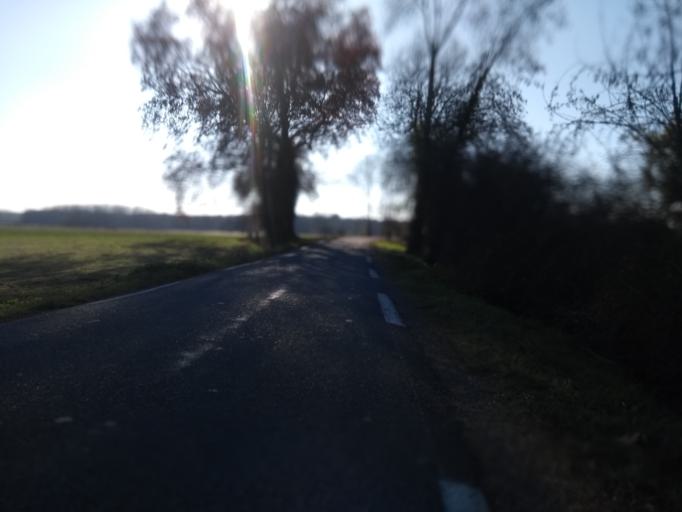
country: FR
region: Aquitaine
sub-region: Departement de la Gironde
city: Ayguemorte-les-Graves
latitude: 44.7237
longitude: -0.4837
